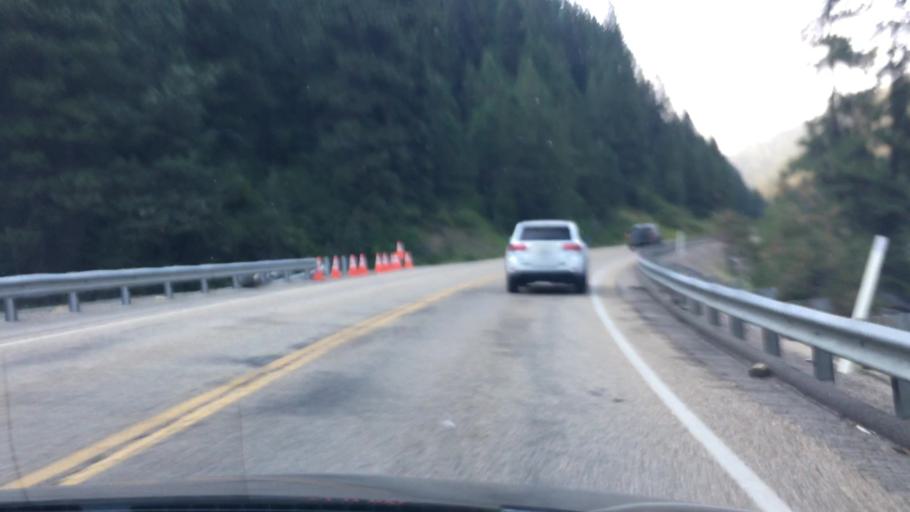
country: US
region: Idaho
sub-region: Valley County
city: Cascade
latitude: 44.1976
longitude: -116.1136
